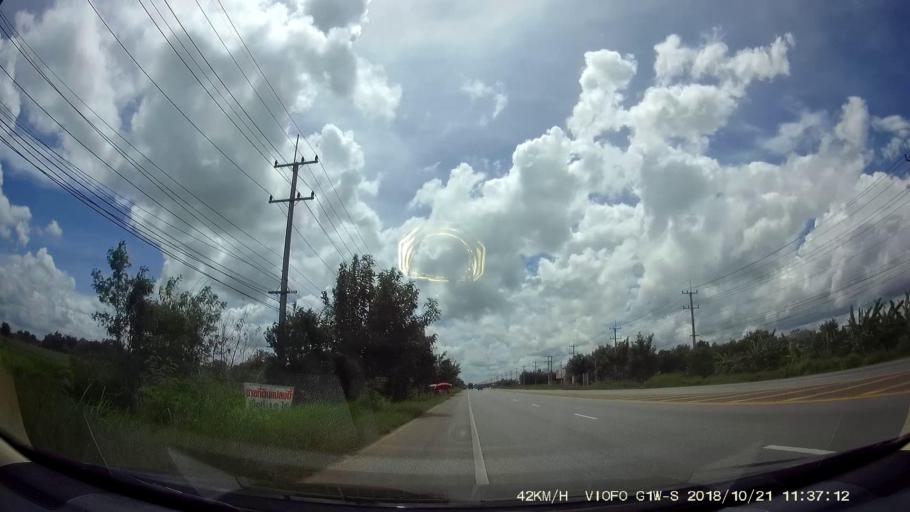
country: TH
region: Chaiyaphum
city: Chaiyaphum
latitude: 15.7165
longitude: 102.0161
